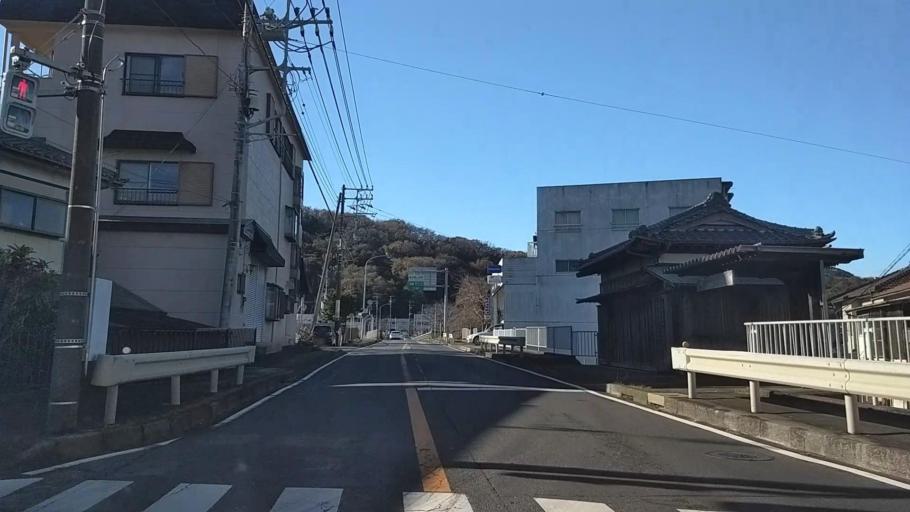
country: JP
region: Chiba
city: Futtsu
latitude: 35.2159
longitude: 139.8703
